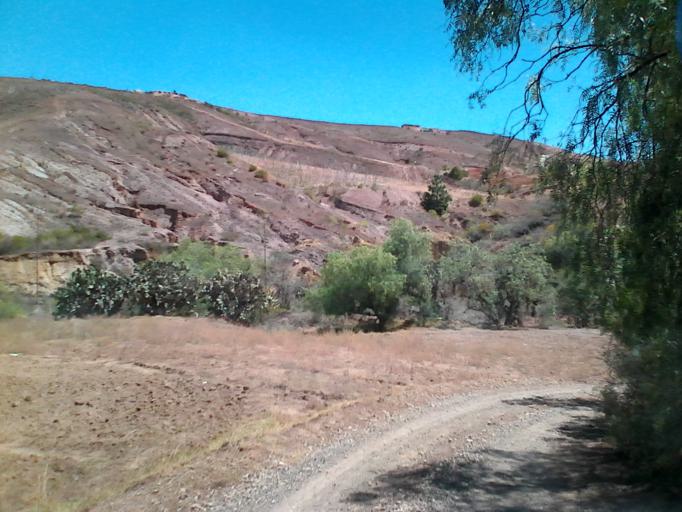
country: CO
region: Boyaca
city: Sachica
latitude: 5.5976
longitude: -73.5662
